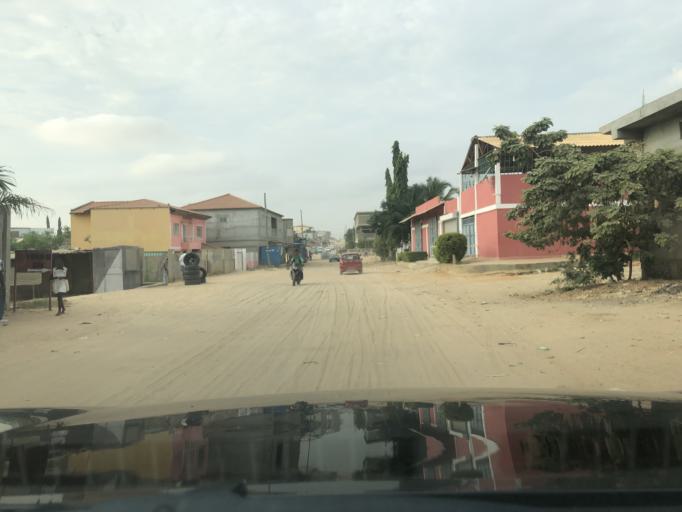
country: AO
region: Luanda
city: Luanda
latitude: -8.9218
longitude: 13.2261
